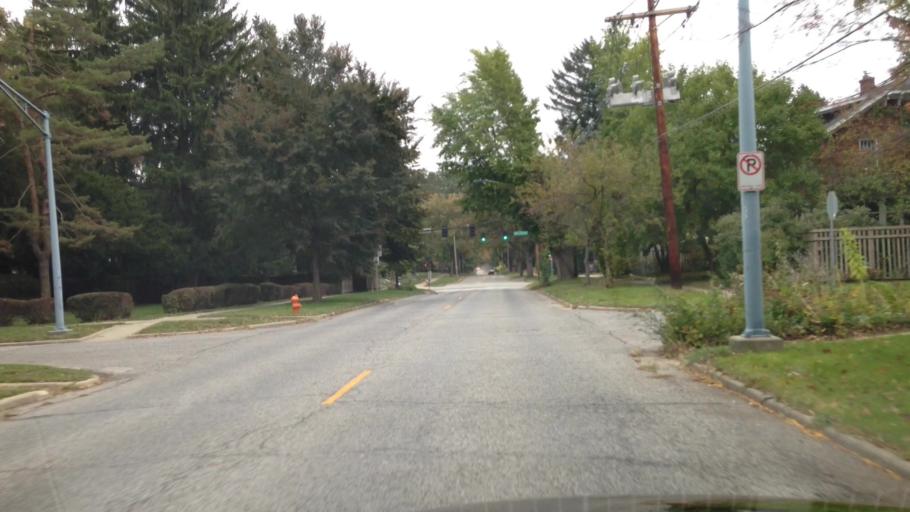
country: US
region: Illinois
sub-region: Champaign County
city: Champaign
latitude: 40.1101
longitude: -88.2592
